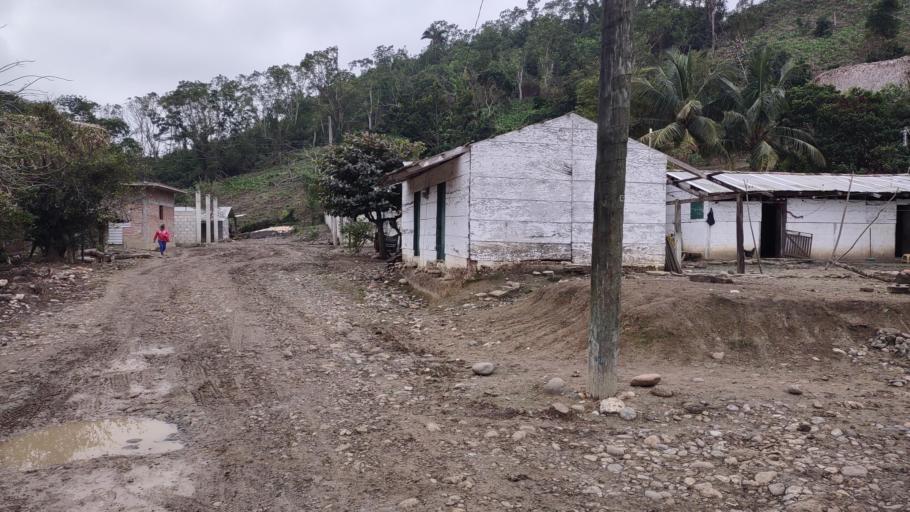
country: MX
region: Veracruz
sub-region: Coatzintla
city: Manuel Maria Contreras
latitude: 20.3986
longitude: -97.4403
